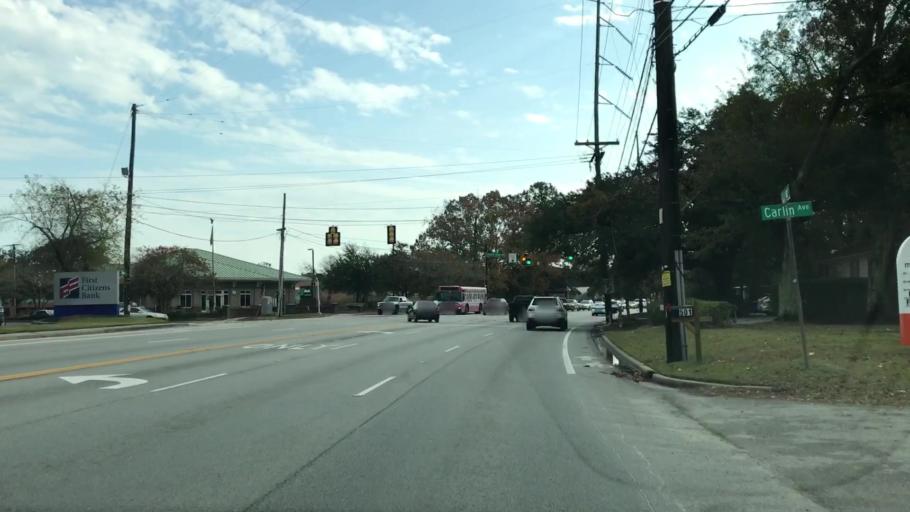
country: US
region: South Carolina
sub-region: Charleston County
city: Charleston
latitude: 32.7554
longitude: -79.9727
